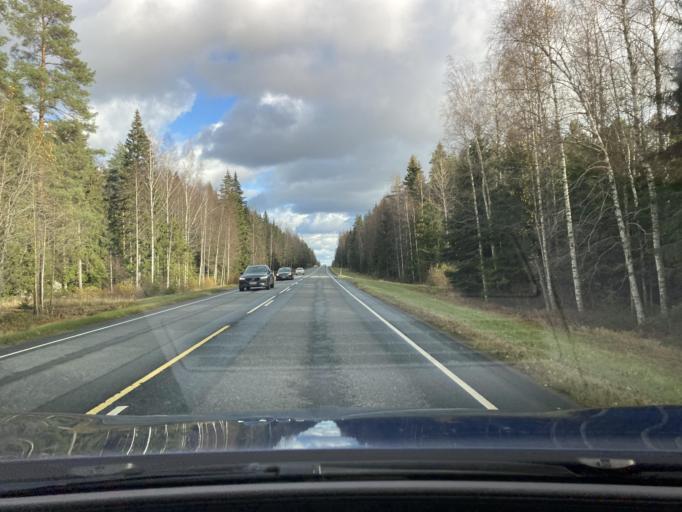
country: FI
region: Haeme
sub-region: Forssa
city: Humppila
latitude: 60.9369
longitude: 23.2654
